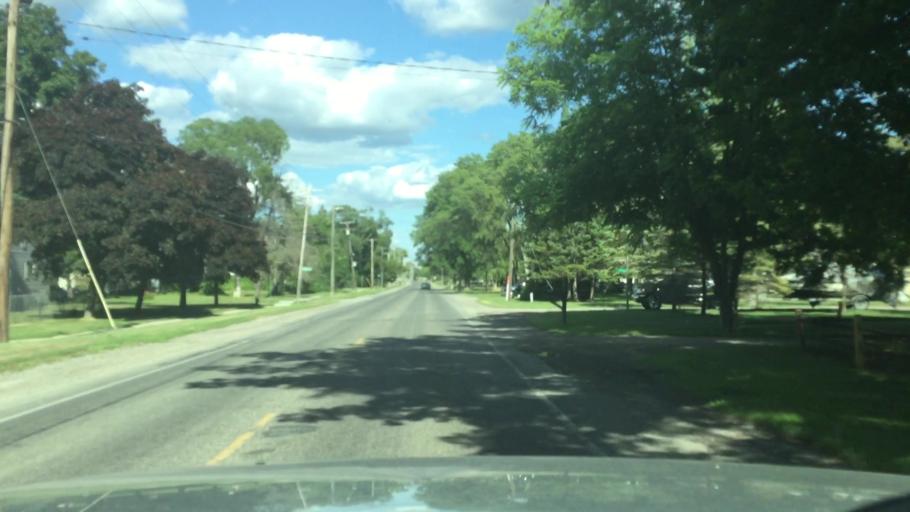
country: US
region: Michigan
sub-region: Saginaw County
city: Shields
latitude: 43.4008
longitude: -84.0052
